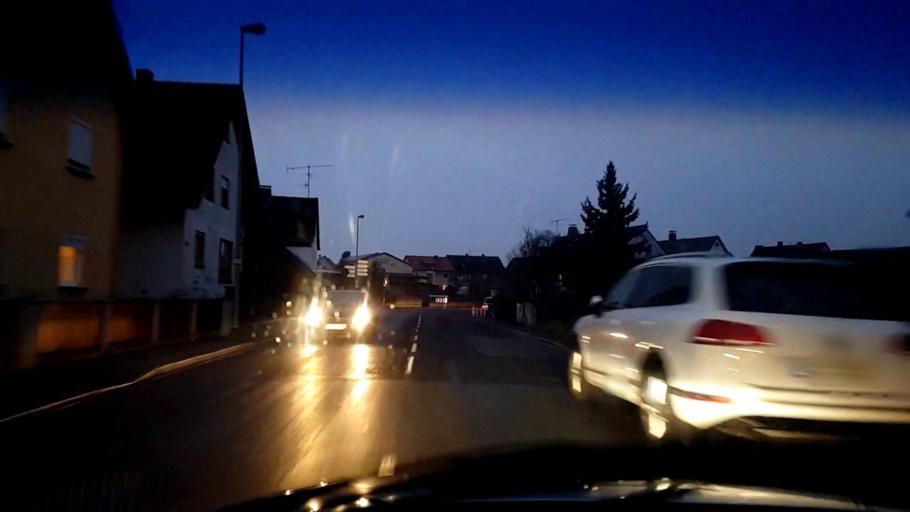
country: DE
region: Bavaria
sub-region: Upper Franconia
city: Hallstadt
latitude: 49.9320
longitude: 10.8818
